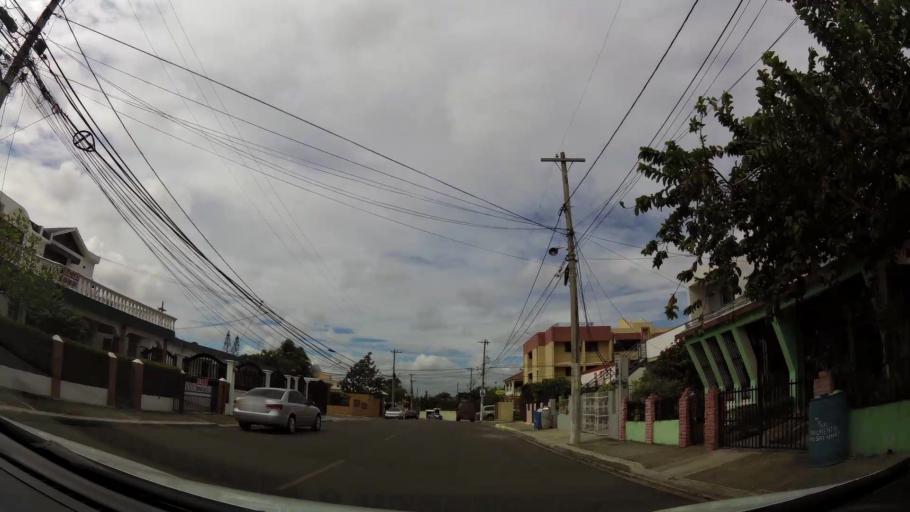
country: DO
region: Santiago
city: Santiago de los Caballeros
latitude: 19.4419
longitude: -70.6739
